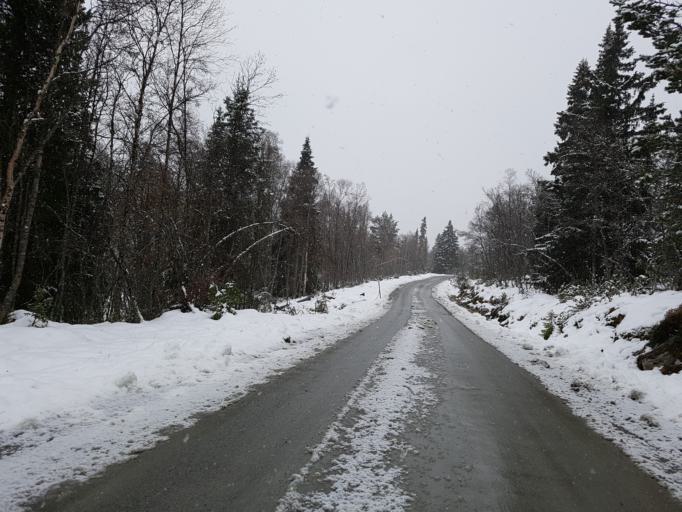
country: NO
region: Oppland
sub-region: Sel
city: Otta
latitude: 61.7922
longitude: 9.7181
